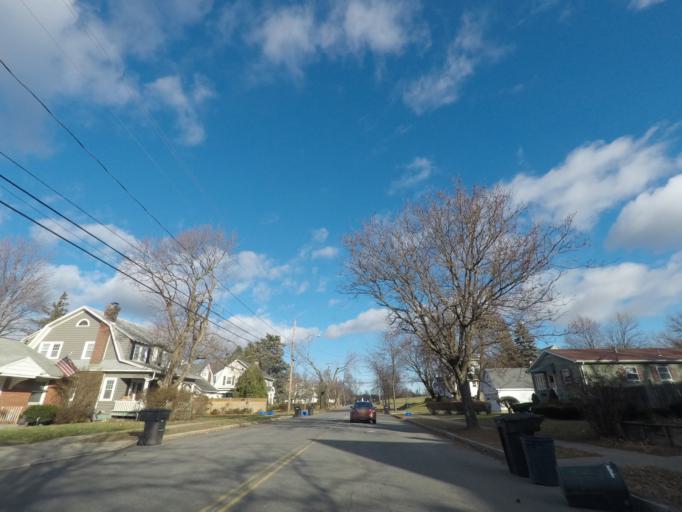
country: US
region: New York
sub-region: Albany County
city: Green Island
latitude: 42.7436
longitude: -73.6736
